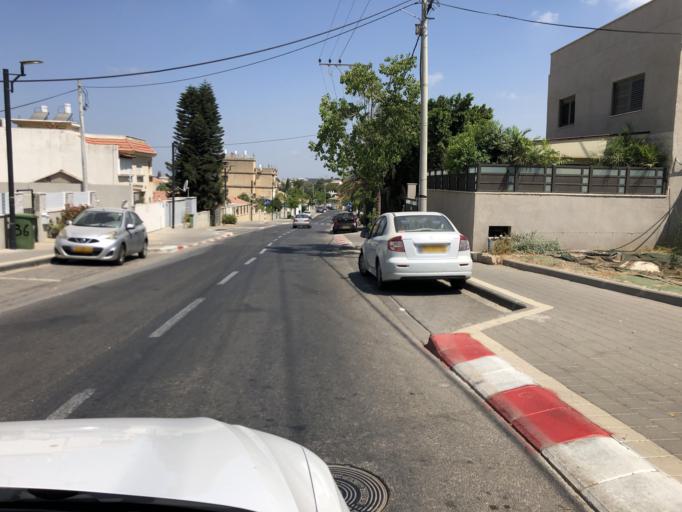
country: IL
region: Central District
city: Rosh Ha'Ayin
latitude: 32.0962
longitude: 34.9571
